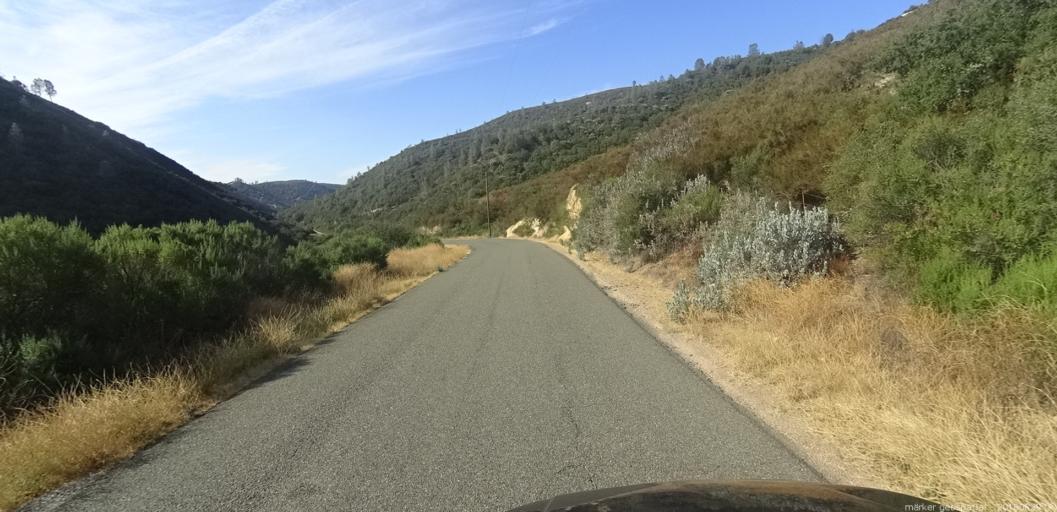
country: US
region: California
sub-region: Monterey County
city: King City
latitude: 36.0157
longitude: -121.0678
